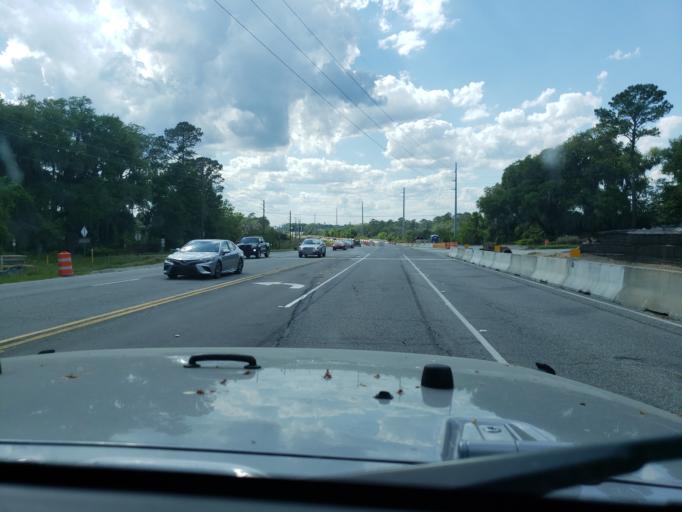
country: US
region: Georgia
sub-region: Chatham County
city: Thunderbolt
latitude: 32.0634
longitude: -81.0325
